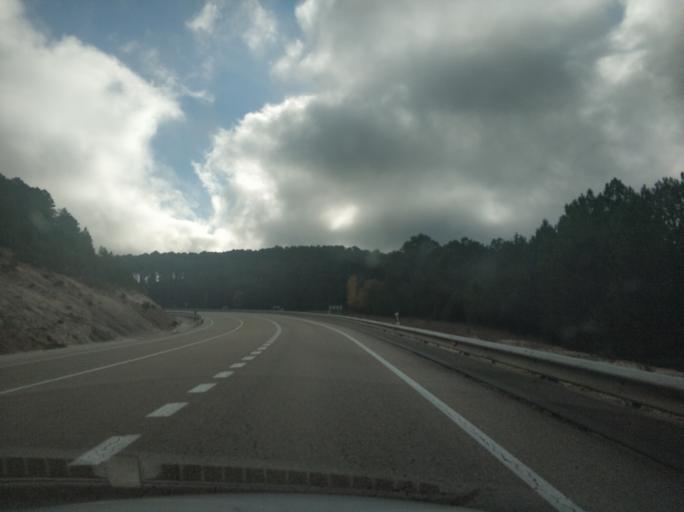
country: ES
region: Castille and Leon
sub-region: Provincia de Soria
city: Navaleno
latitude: 41.8288
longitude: -2.9673
